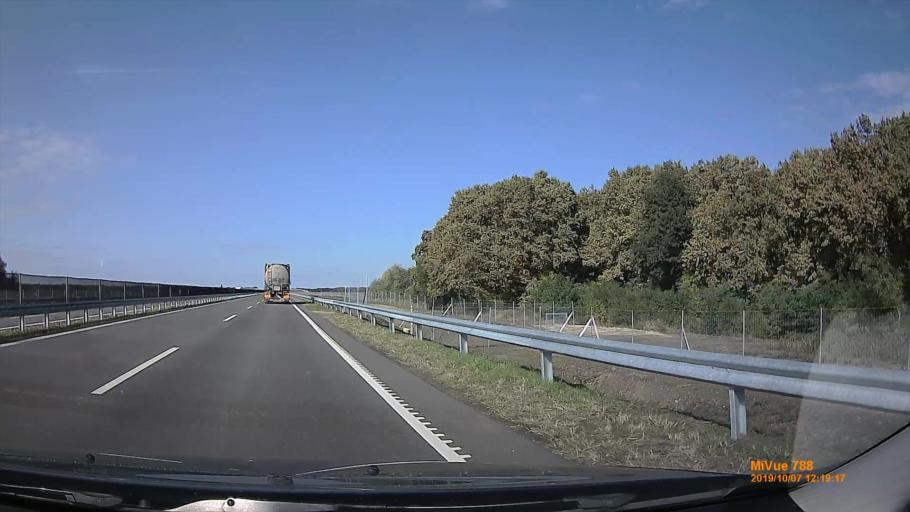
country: HU
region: Jasz-Nagykun-Szolnok
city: Kunszentmarton
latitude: 46.8460
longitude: 20.3288
